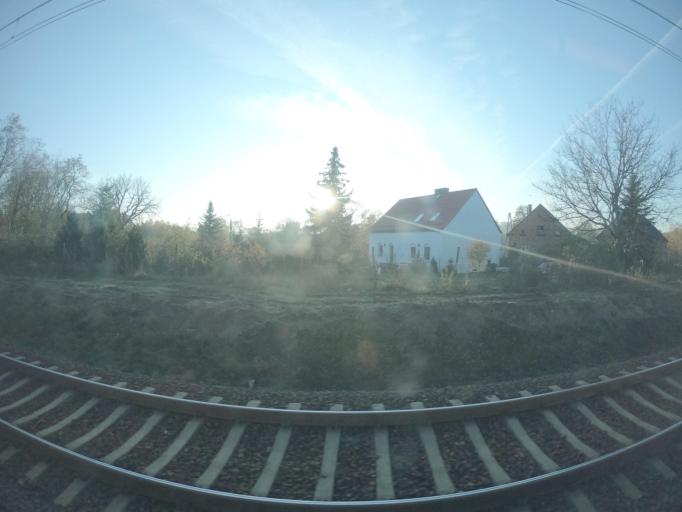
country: PL
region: Lubusz
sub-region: Powiat sulecinski
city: Torzym
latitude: 52.2551
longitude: 14.9516
